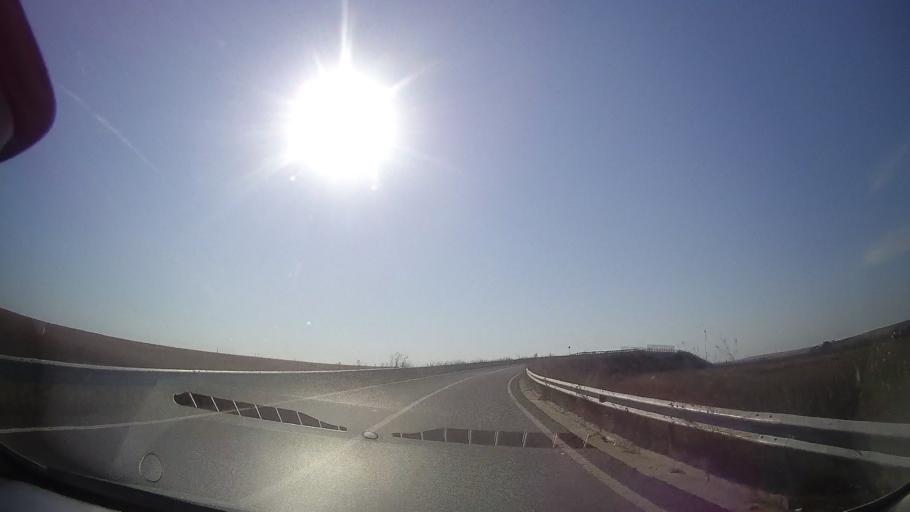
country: RO
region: Timis
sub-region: Comuna Topolovatu Mare
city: Topolovatu Mare
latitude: 45.8074
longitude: 21.5844
